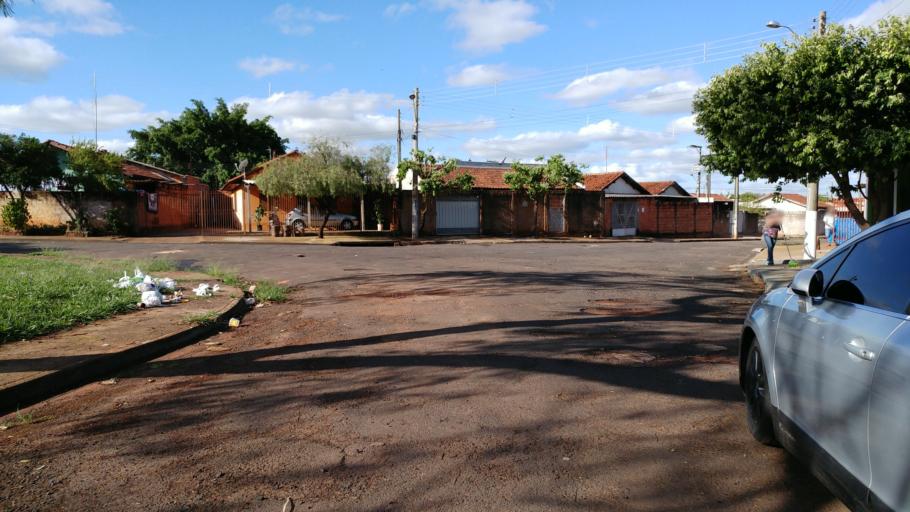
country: BR
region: Sao Paulo
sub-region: Paraguacu Paulista
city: Paraguacu Paulista
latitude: -22.4354
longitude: -50.5749
